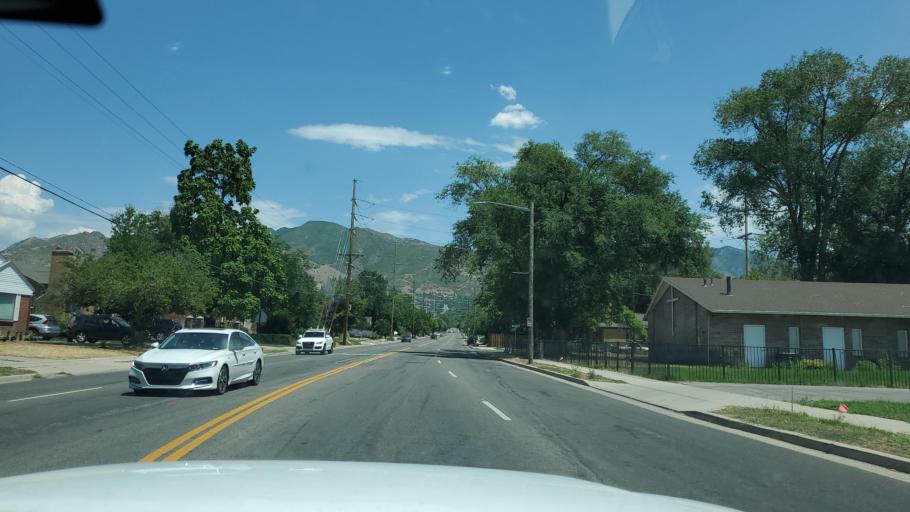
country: US
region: Utah
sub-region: Salt Lake County
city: Willard
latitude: 40.7254
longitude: -111.8417
